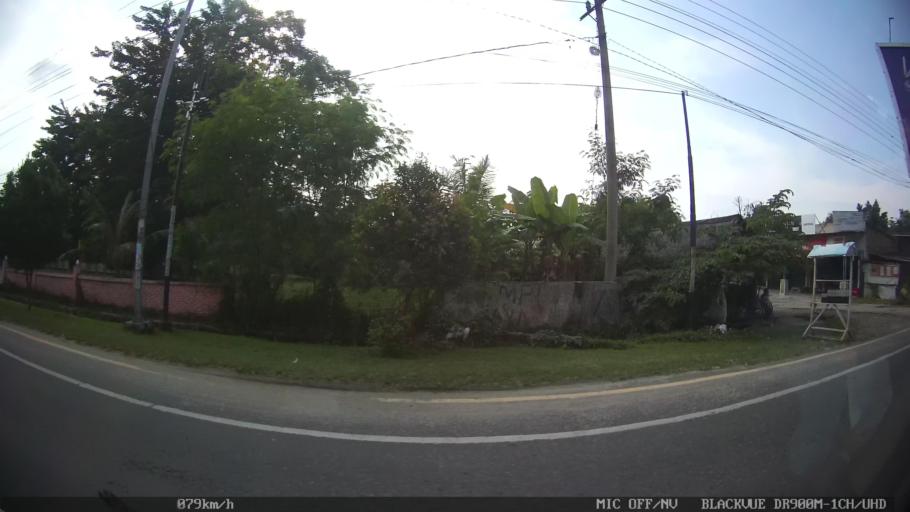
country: ID
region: North Sumatra
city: Percut
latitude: 3.5724
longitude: 98.7985
